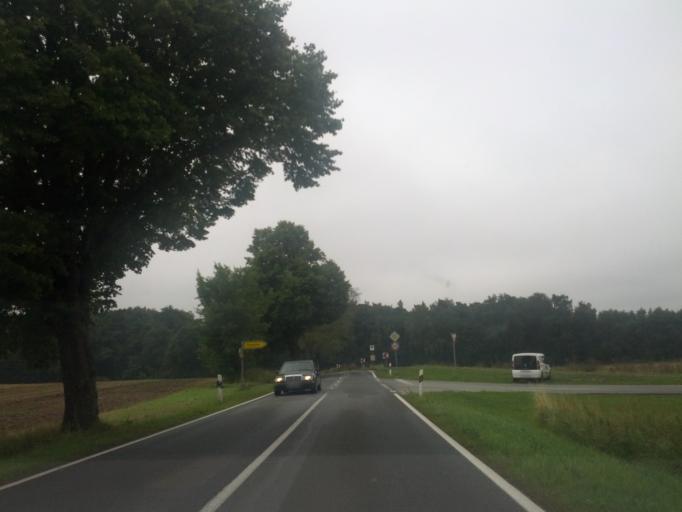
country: DE
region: Mecklenburg-Vorpommern
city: Neubukow
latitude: 54.0465
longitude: 11.6661
